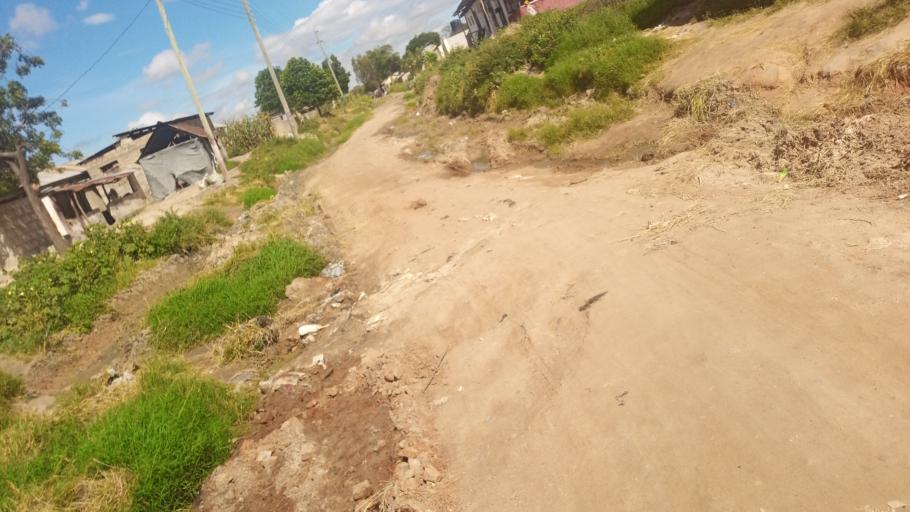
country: TZ
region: Dodoma
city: Dodoma
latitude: -6.1884
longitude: 35.7272
